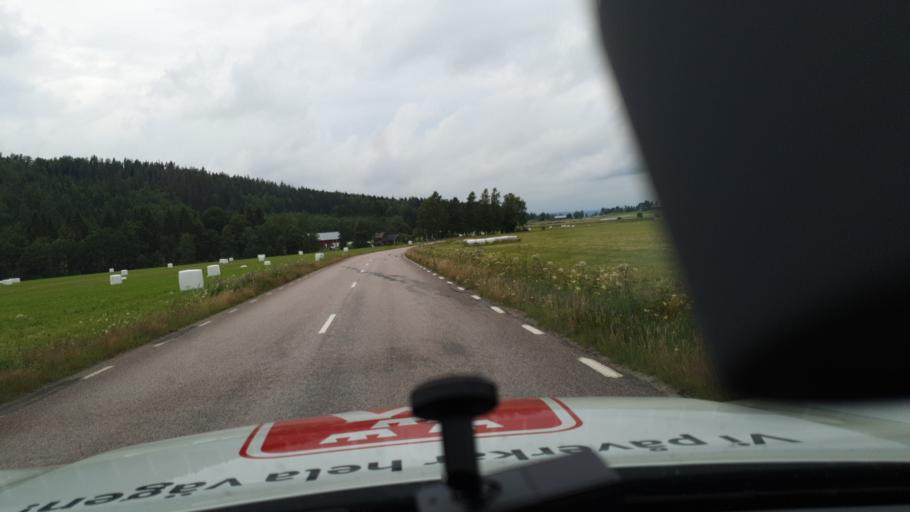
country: SE
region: Vaermland
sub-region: Sunne Kommun
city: Sunne
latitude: 59.8121
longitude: 13.2257
